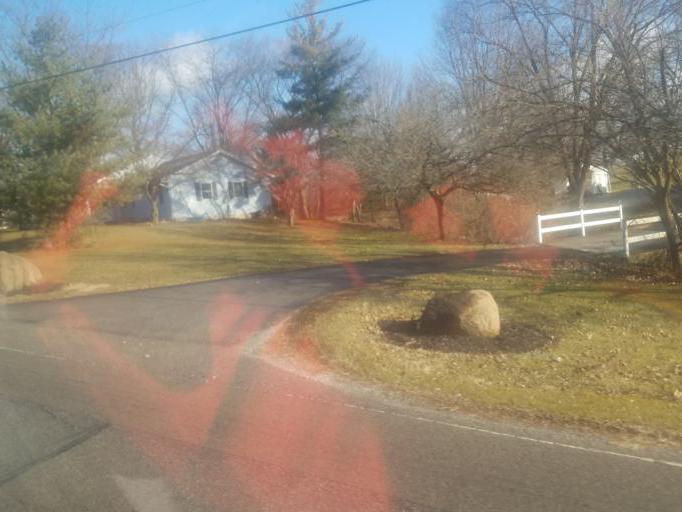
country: US
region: Ohio
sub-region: Marion County
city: Marion
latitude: 40.5485
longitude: -83.1576
